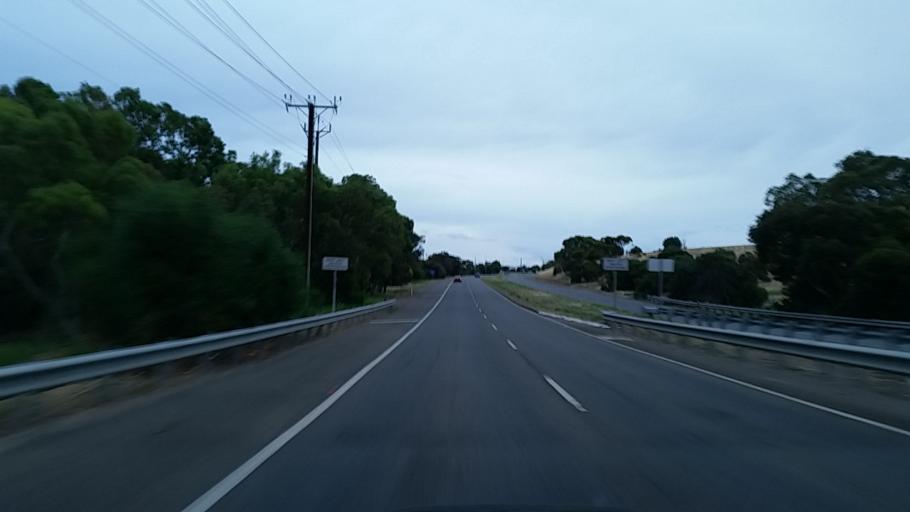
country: AU
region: South Australia
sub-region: Adelaide
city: Port Noarlunga
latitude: -35.1237
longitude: 138.4870
